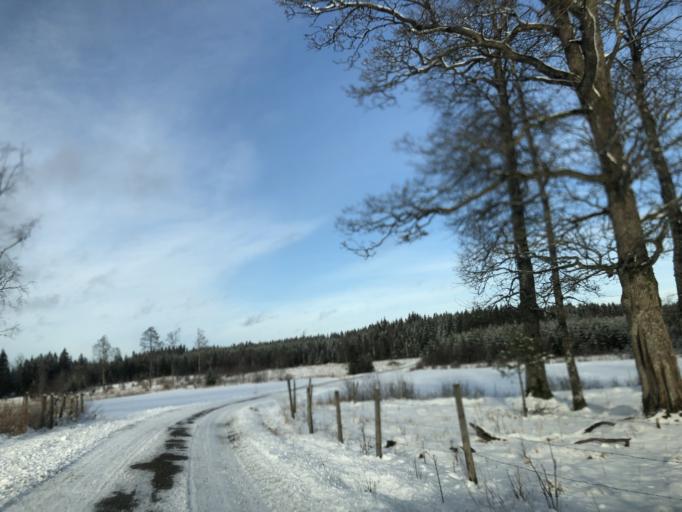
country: SE
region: Vaestra Goetaland
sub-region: Ulricehamns Kommun
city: Ulricehamn
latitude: 57.7374
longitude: 13.4924
